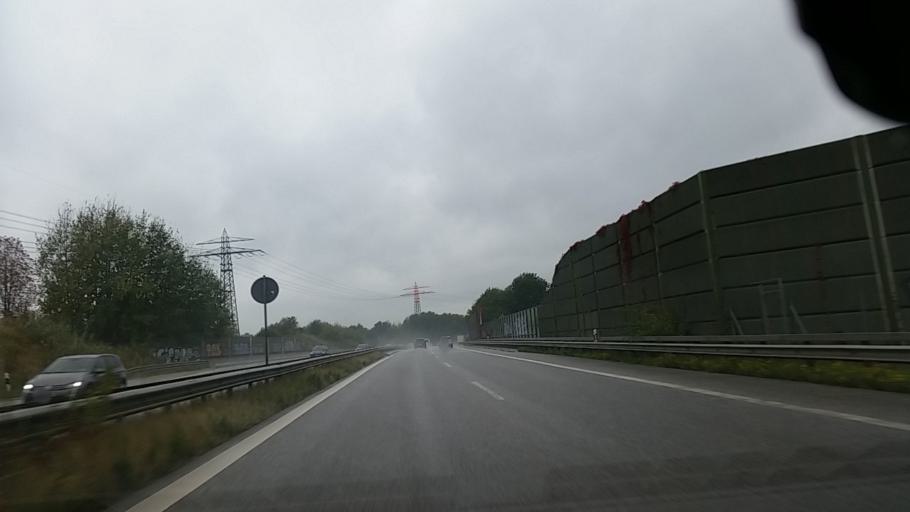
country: DE
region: Schleswig-Holstein
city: Oststeinbek
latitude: 53.4852
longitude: 10.1238
